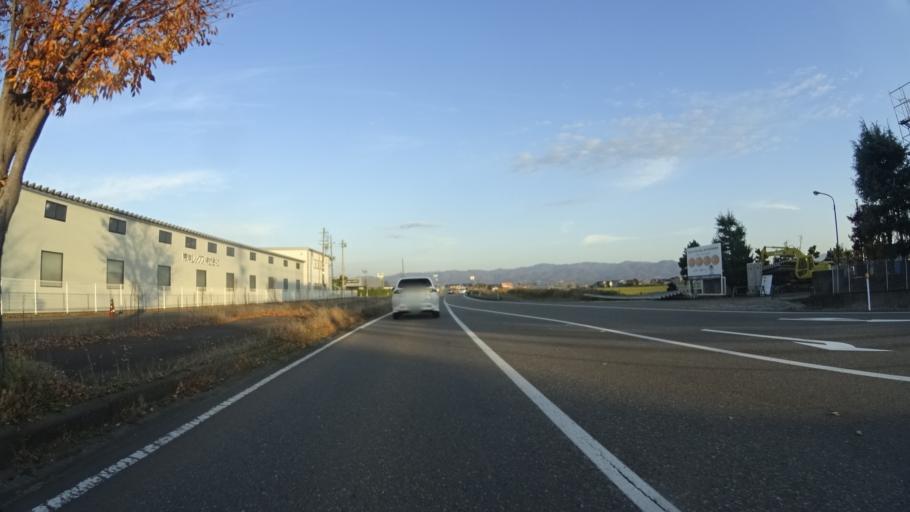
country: JP
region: Niigata
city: Nagaoka
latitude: 37.4378
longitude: 138.7986
